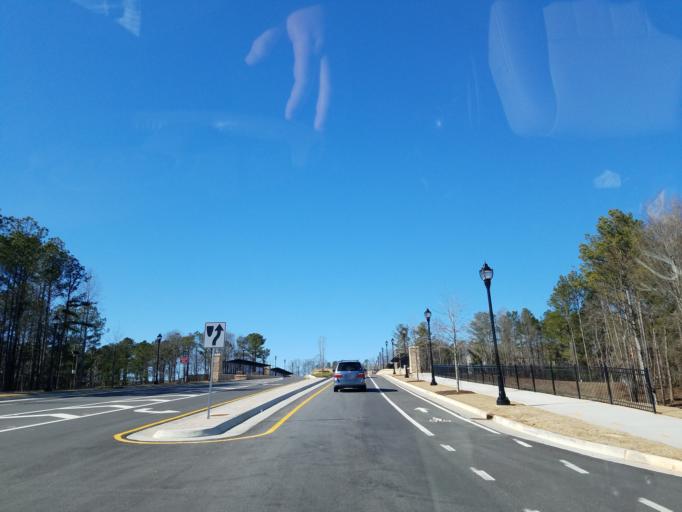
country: US
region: Georgia
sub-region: Fulton County
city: Alpharetta
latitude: 34.0465
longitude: -84.3020
